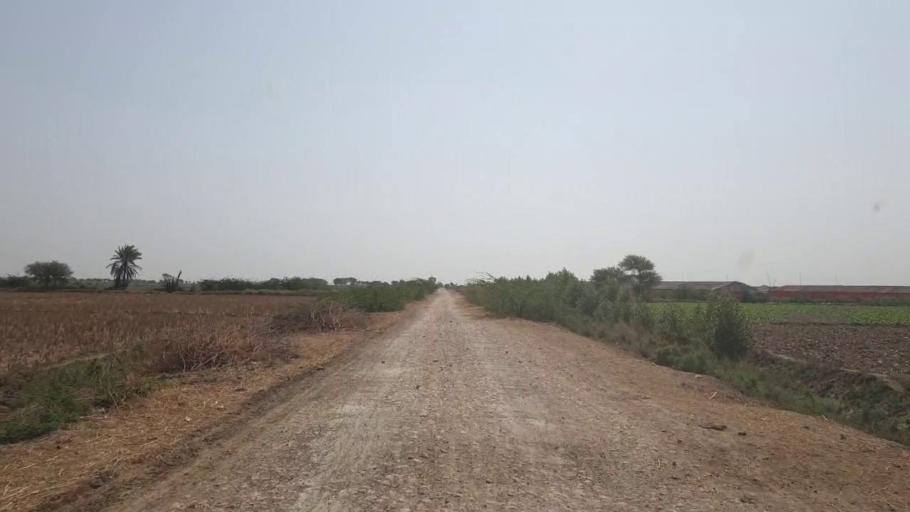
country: PK
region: Sindh
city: Jati
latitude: 24.4263
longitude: 68.5524
